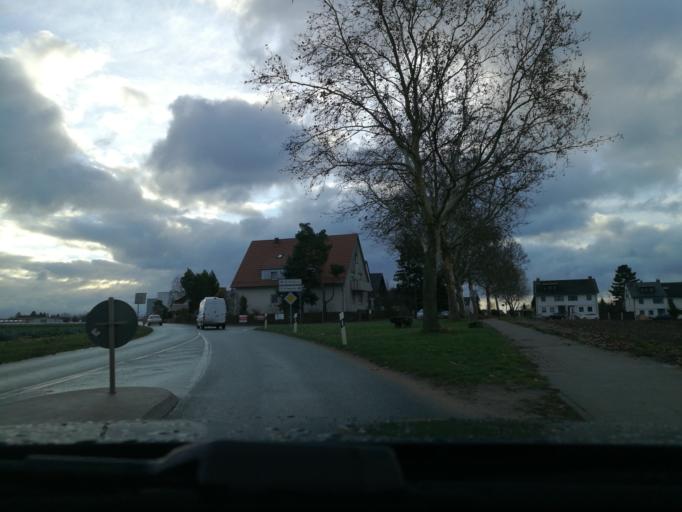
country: DE
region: Bavaria
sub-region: Regierungsbezirk Mittelfranken
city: Wetzendorf
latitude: 49.4787
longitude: 11.0208
